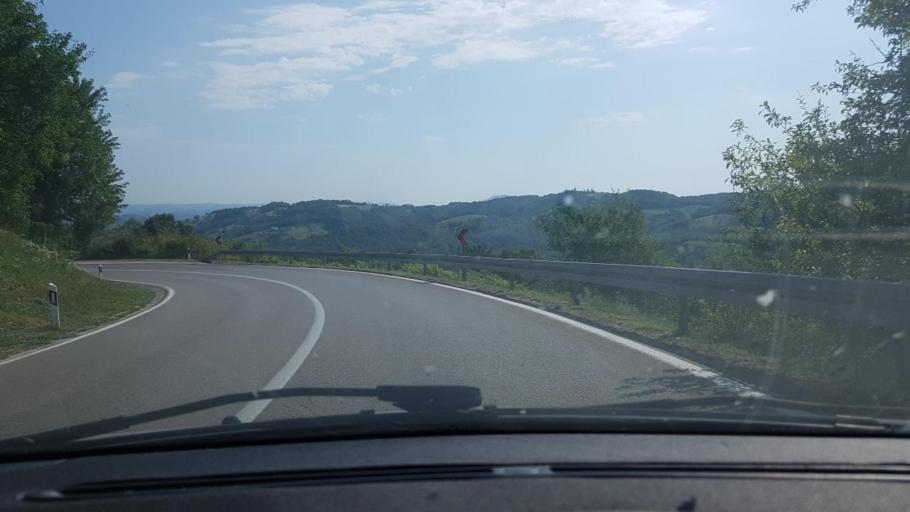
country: BA
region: Federation of Bosnia and Herzegovina
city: Skokovi
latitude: 45.0359
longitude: 15.9194
